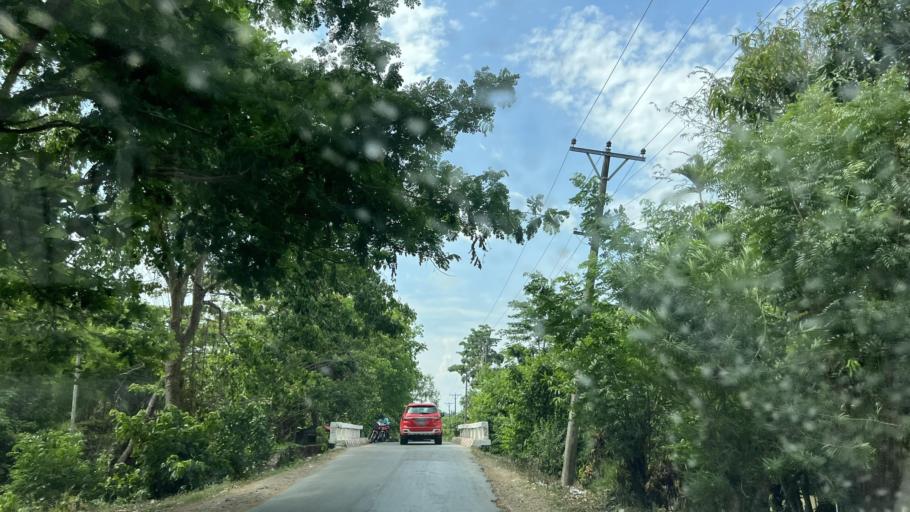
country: MM
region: Ayeyarwady
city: Pyapon
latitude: 16.2547
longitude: 95.7025
